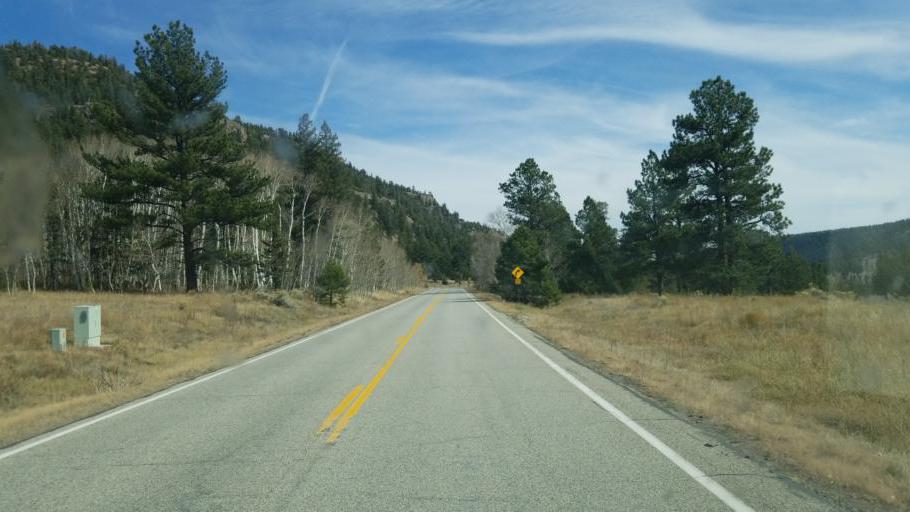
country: US
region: Colorado
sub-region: Conejos County
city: Conejos
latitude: 37.0748
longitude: -106.2701
